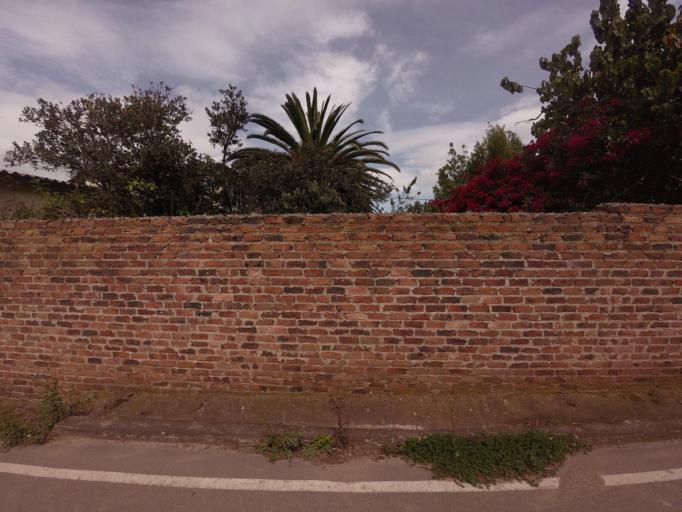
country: CO
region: Boyaca
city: Nobsa
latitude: 5.7907
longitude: -72.9736
